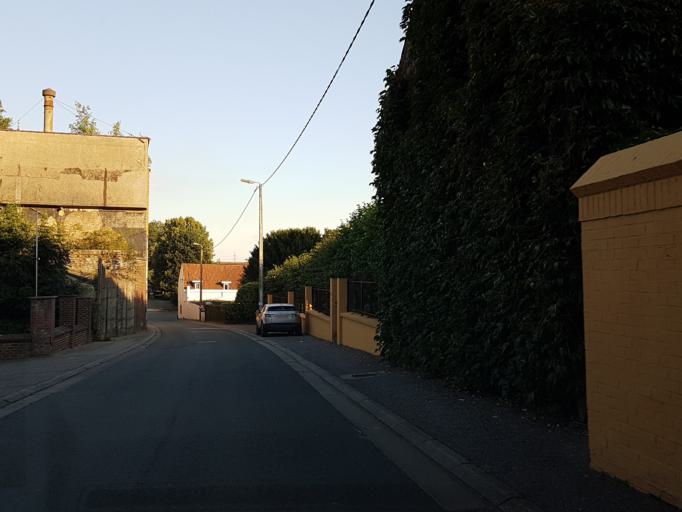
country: BE
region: Flanders
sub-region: Provincie Vlaams-Brabant
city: Merchtem
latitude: 50.9111
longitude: 4.2489
